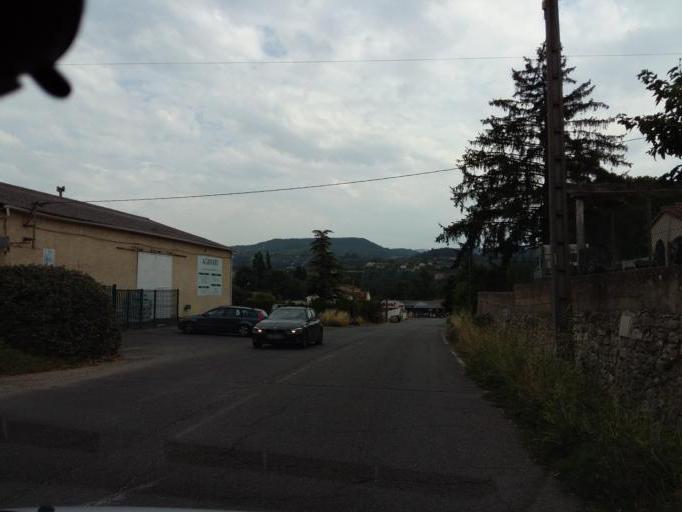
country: FR
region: Provence-Alpes-Cote d'Azur
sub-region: Departement du Vaucluse
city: Apt
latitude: 43.8866
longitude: 5.3766
